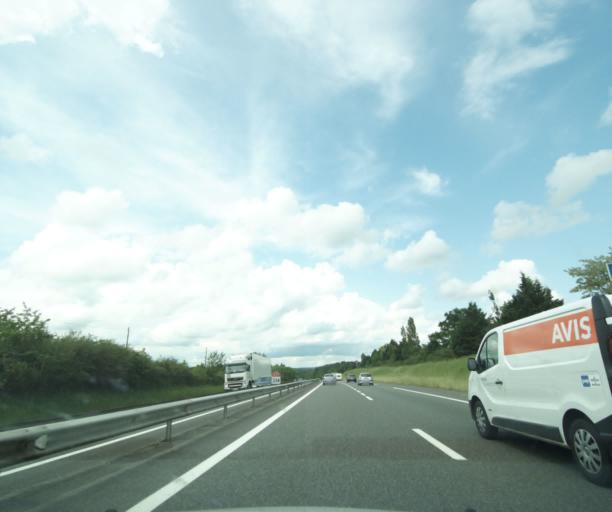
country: FR
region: Auvergne
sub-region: Departement de l'Allier
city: Bellenaves
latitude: 46.2247
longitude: 3.1001
